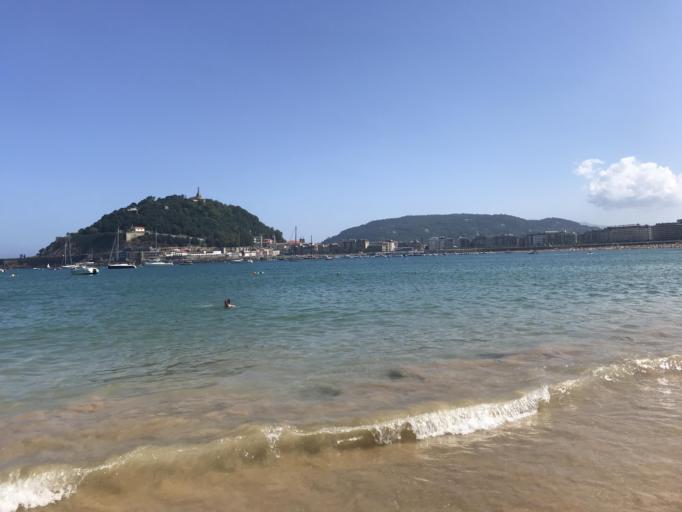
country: ES
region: Basque Country
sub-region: Provincia de Guipuzcoa
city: San Sebastian
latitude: 43.3161
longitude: -1.9981
